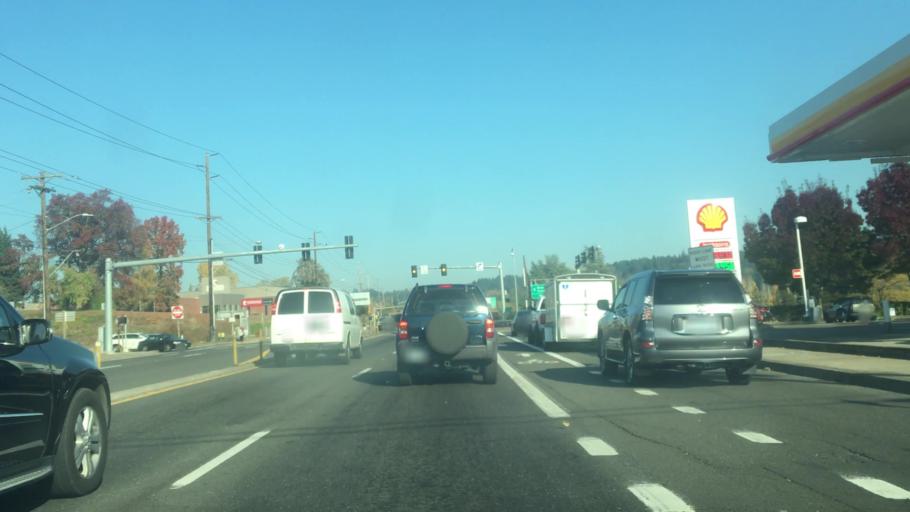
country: US
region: Oregon
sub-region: Washington County
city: Tigard
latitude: 45.4345
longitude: -122.7633
